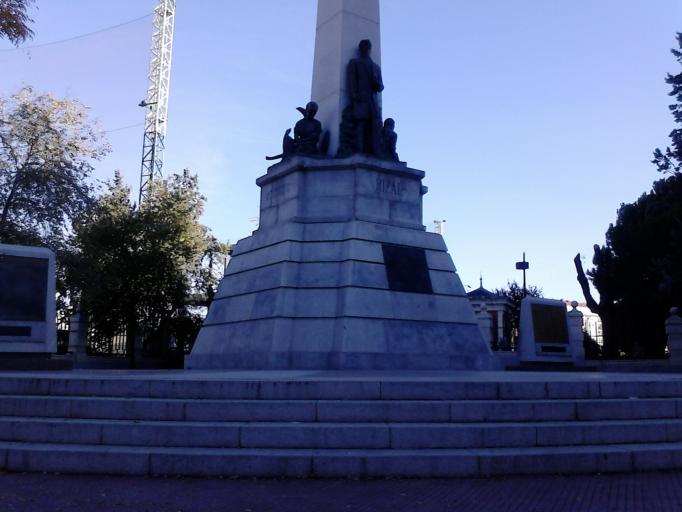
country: ES
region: Madrid
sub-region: Provincia de Madrid
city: Chamberi
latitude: 40.4411
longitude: -3.7080
